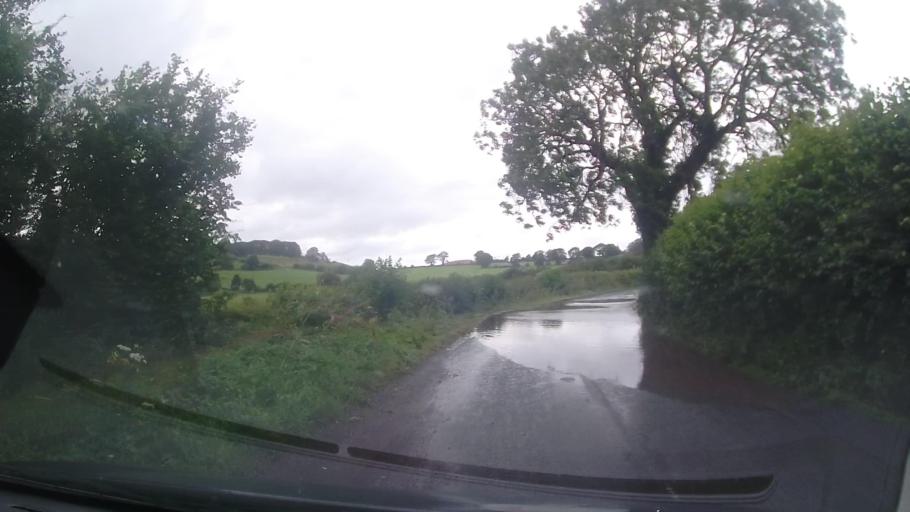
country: GB
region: England
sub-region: Shropshire
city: Pontesbury
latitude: 52.5852
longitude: -2.8817
